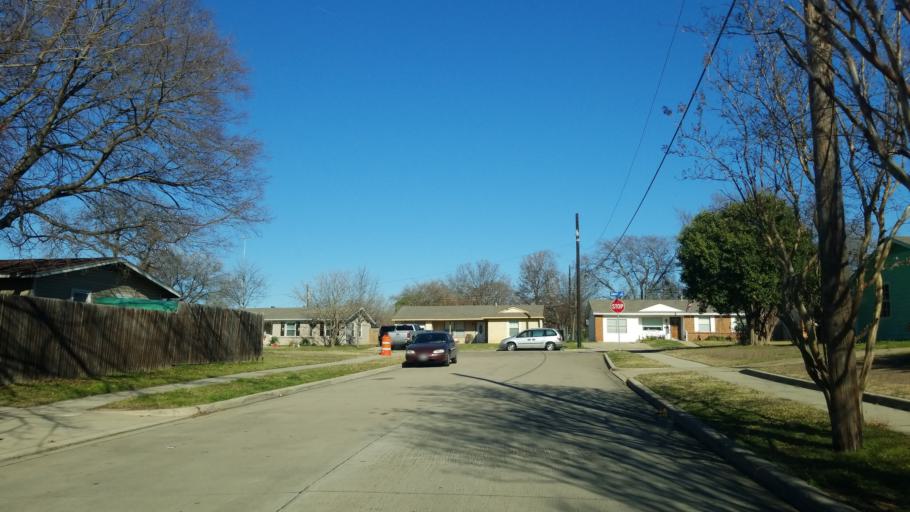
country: US
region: Texas
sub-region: Tarrant County
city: Arlington
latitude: 32.7294
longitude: -97.0612
